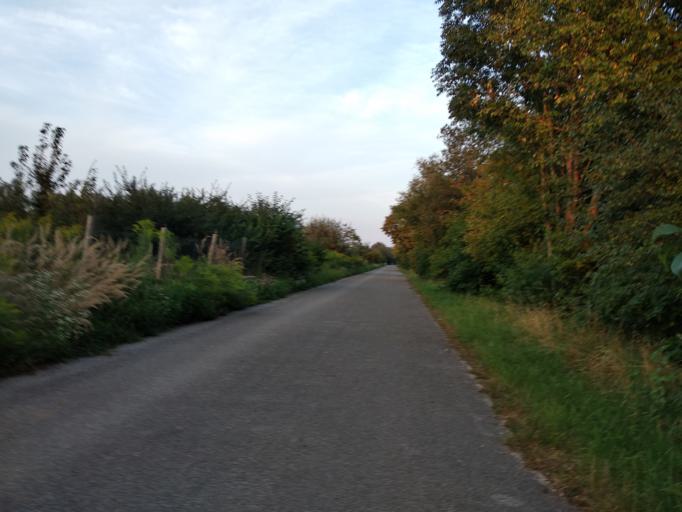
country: DE
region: Bavaria
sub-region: Upper Bavaria
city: Vaterstetten
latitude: 48.1425
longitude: 11.7750
